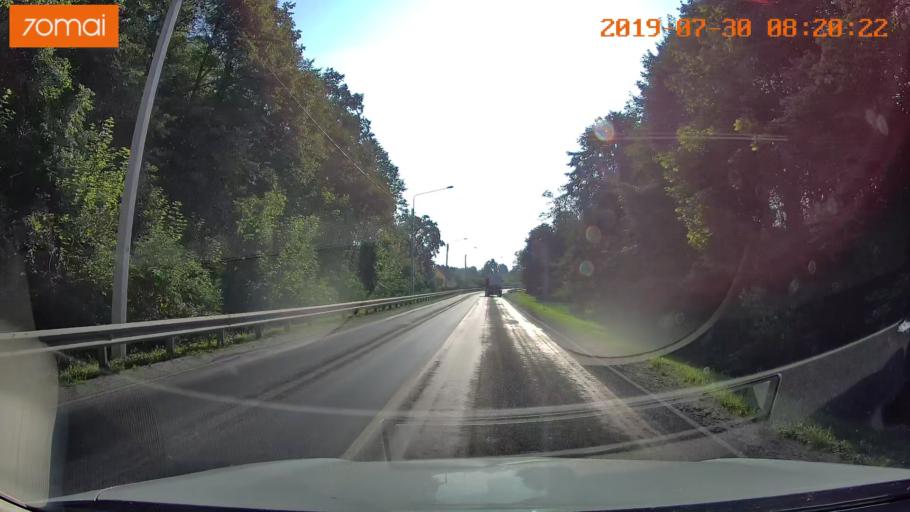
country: RU
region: Kaliningrad
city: Chernyakhovsk
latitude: 54.6266
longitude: 21.5140
